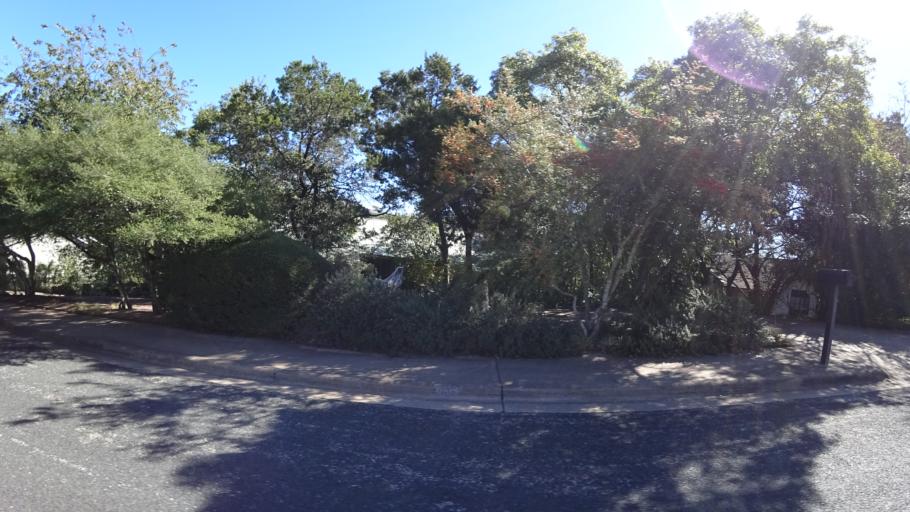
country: US
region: Texas
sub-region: Travis County
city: West Lake Hills
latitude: 30.3504
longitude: -97.7784
